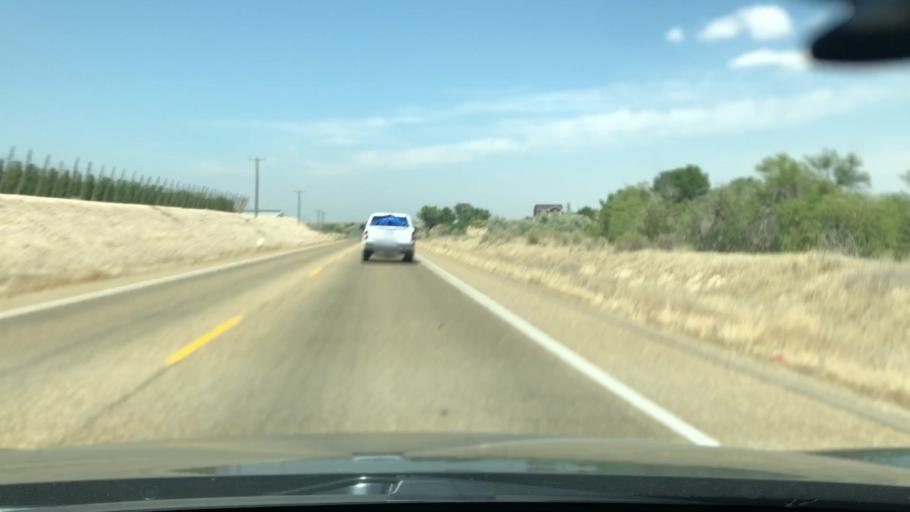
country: US
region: Idaho
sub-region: Canyon County
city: Wilder
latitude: 43.7097
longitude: -116.9119
